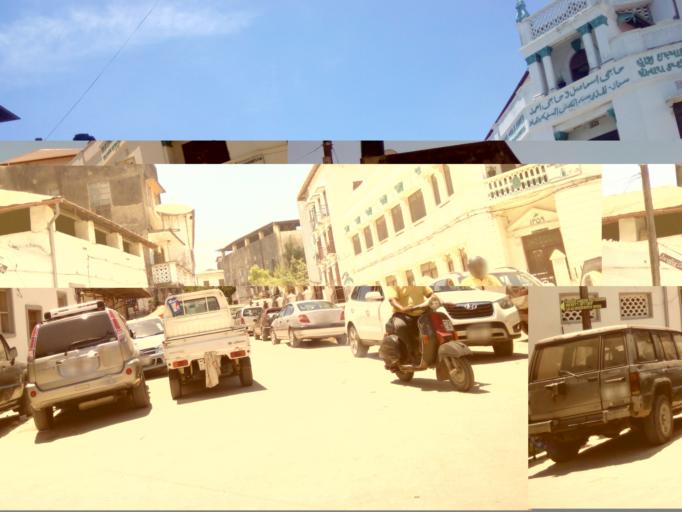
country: TZ
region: Zanzibar Urban/West
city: Zanzibar
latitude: -6.1635
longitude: 39.1913
